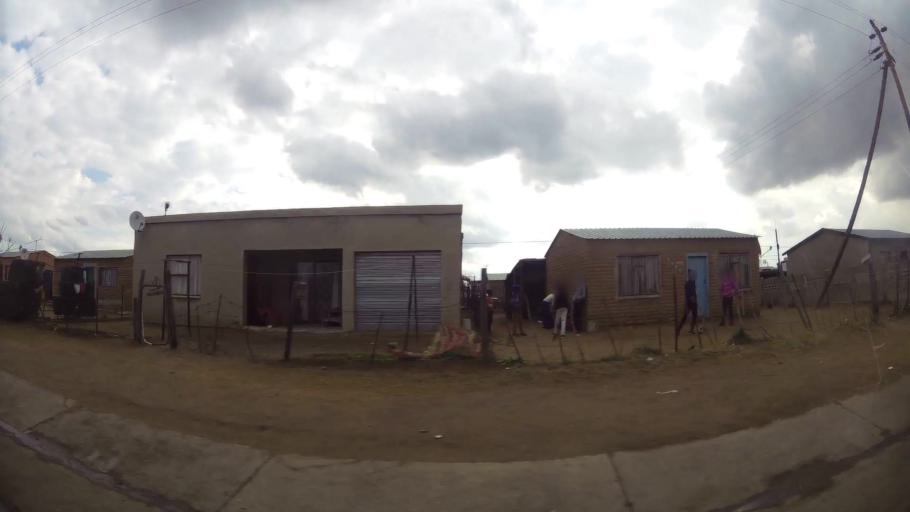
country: ZA
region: Orange Free State
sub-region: Fezile Dabi District Municipality
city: Sasolburg
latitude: -26.8549
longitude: 27.8591
